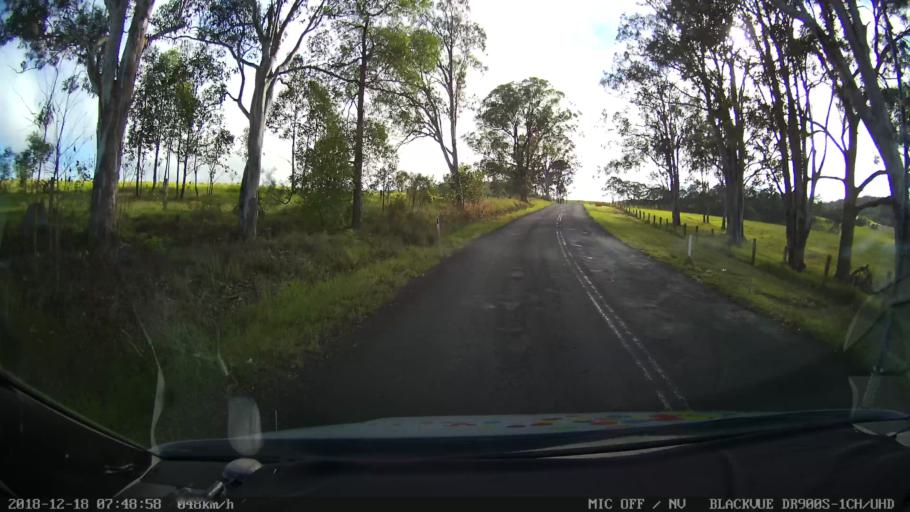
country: AU
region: New South Wales
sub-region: Kyogle
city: Kyogle
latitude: -28.4566
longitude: 152.5674
